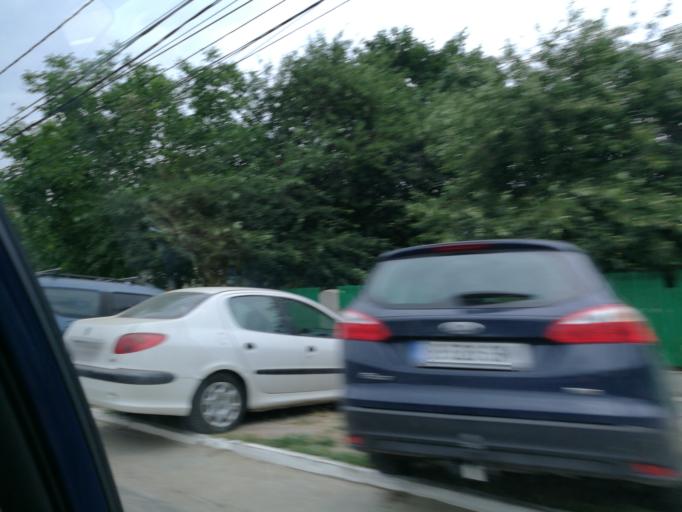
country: RO
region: Constanta
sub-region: Municipiul Mangalia
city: Mangalia
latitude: 43.7835
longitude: 28.5782
